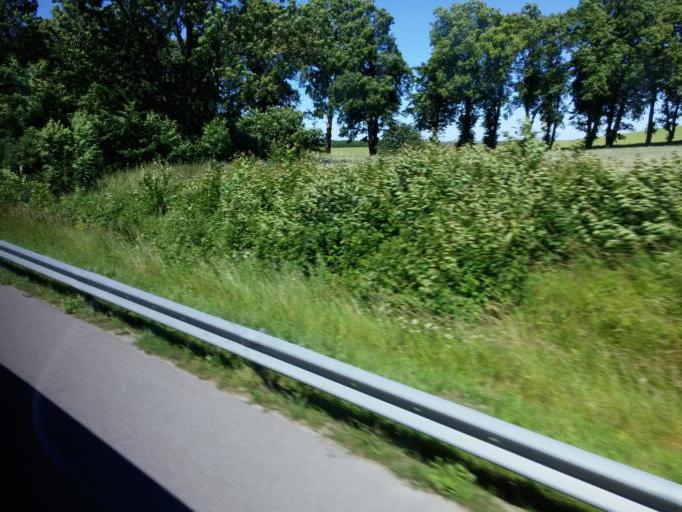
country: SE
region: Skane
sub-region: Malmo
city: Oxie
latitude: 55.5427
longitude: 13.1564
